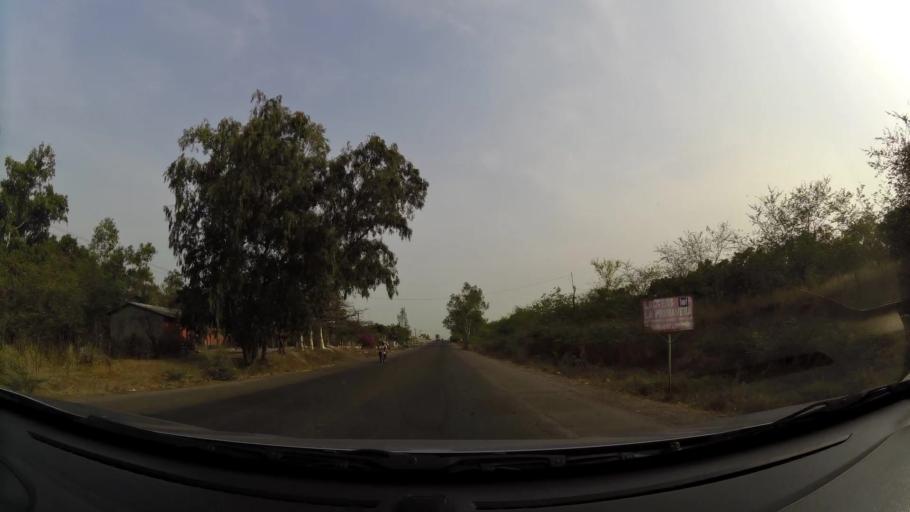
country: HN
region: Comayagua
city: Flores
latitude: 14.3048
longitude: -87.5772
